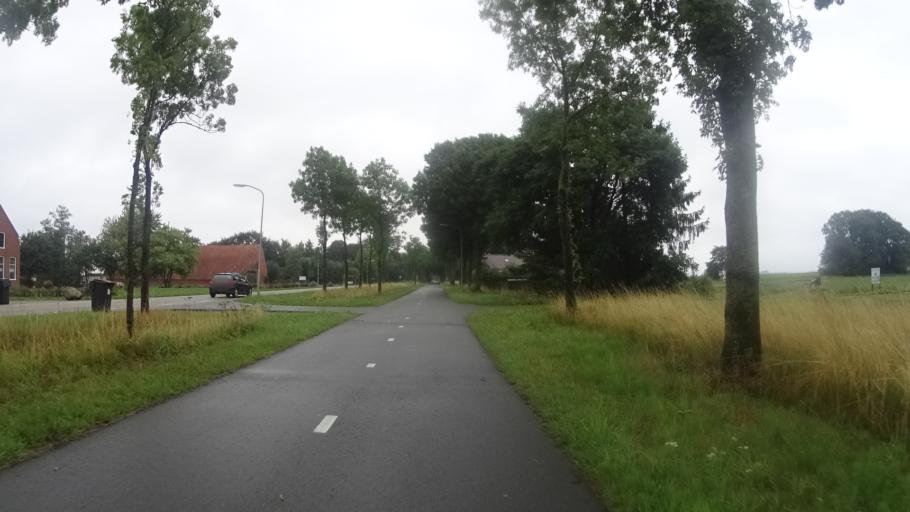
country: NL
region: Groningen
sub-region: Gemeente  Oldambt
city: Winschoten
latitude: 53.1577
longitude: 7.0768
